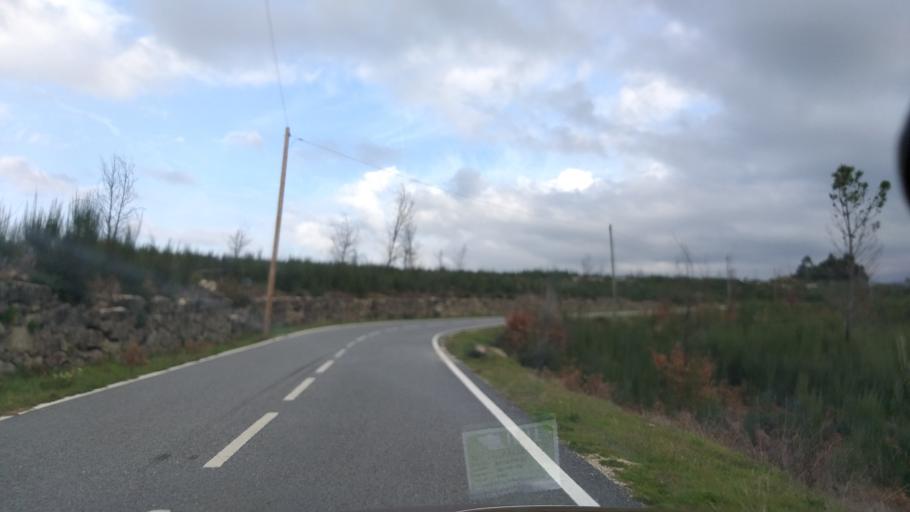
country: PT
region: Guarda
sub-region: Seia
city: Seia
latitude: 40.4851
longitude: -7.6570
